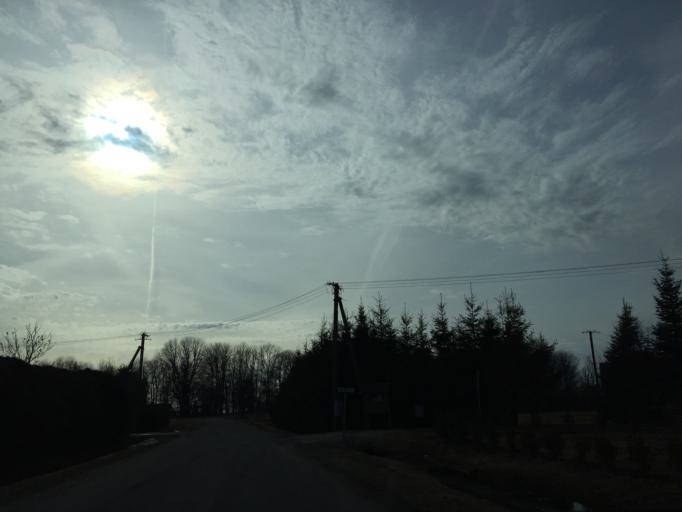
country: EE
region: Paernumaa
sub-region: Paernu linn
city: Parnu
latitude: 58.2456
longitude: 24.4846
